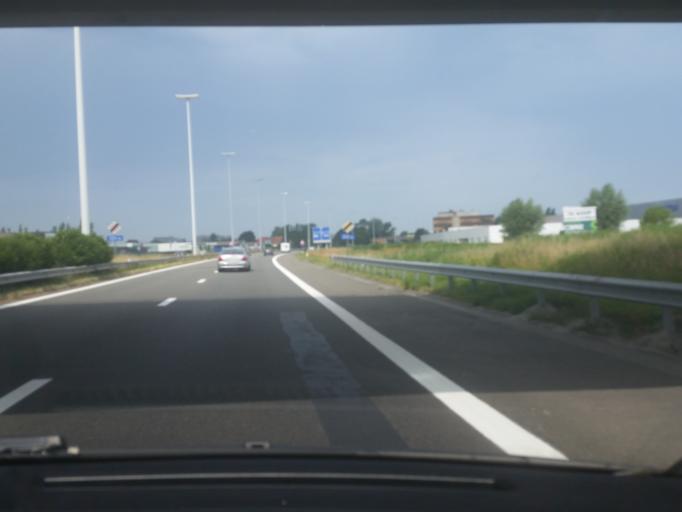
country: BE
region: Flanders
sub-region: Provincie West-Vlaanderen
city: Ostend
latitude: 51.2095
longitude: 2.9424
